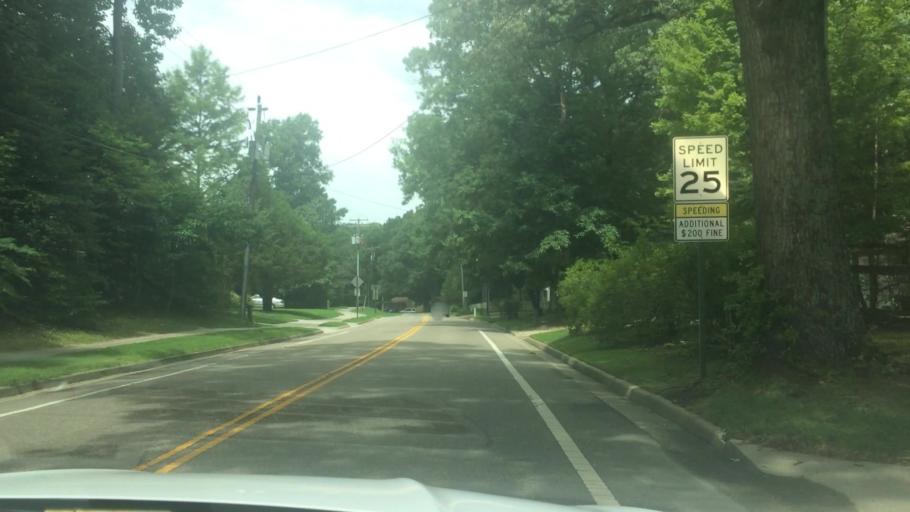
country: US
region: Virginia
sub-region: James City County
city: Williamsburg
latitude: 37.2969
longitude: -76.7322
